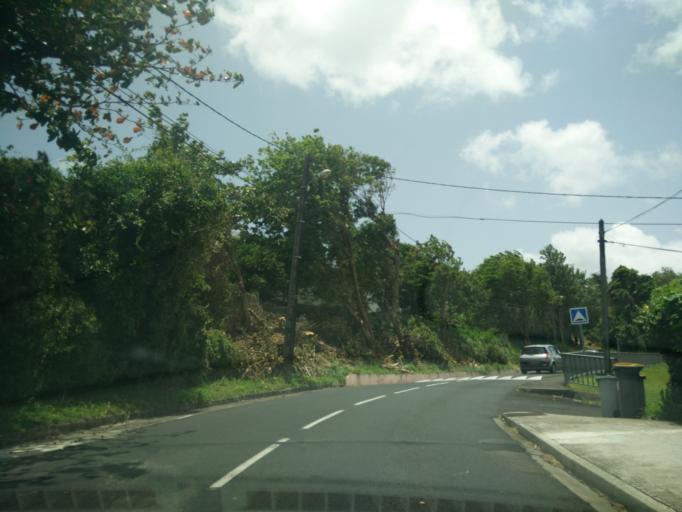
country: MQ
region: Martinique
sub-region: Martinique
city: Fort-de-France
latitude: 14.6315
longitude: -61.0728
